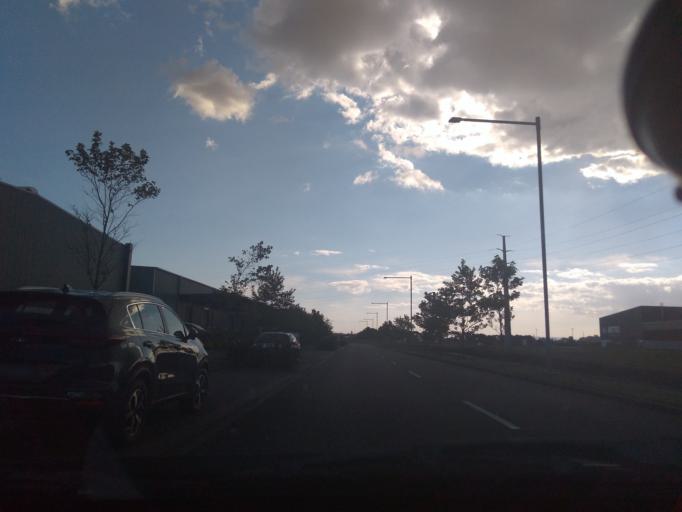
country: NZ
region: Auckland
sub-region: Auckland
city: Tamaki
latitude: -36.9302
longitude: 174.8735
